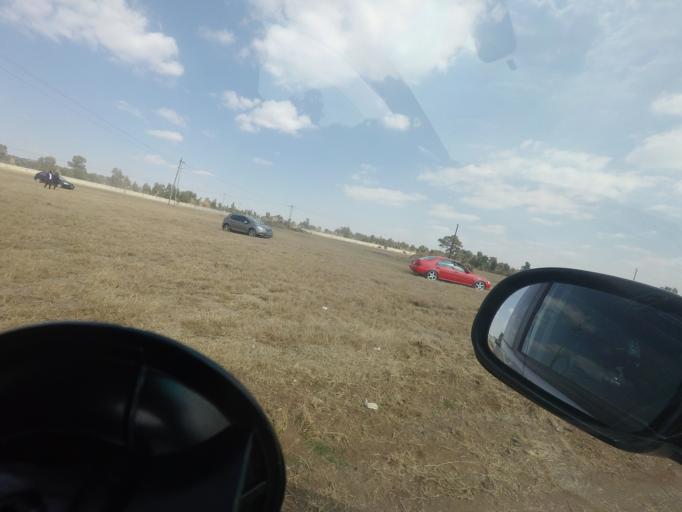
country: ZA
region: Gauteng
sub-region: Sedibeng District Municipality
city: Heidelberg
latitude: -26.5412
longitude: 28.3548
